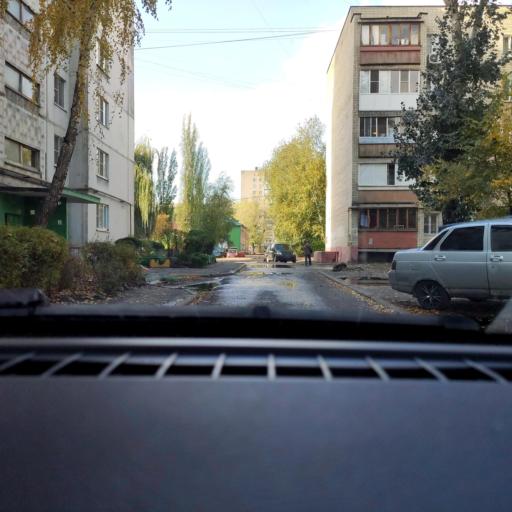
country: RU
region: Voronezj
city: Maslovka
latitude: 51.6387
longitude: 39.2718
